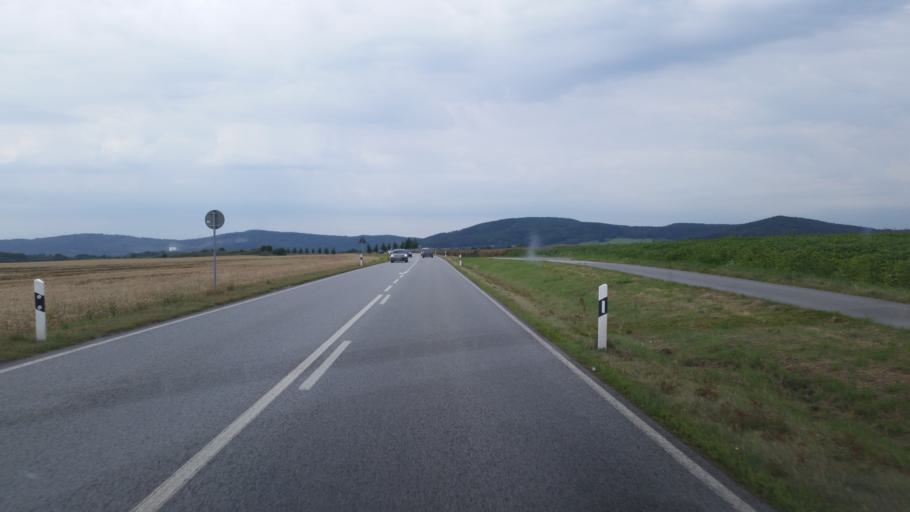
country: DE
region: Saxony
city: Elstra
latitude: 51.2334
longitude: 14.1532
